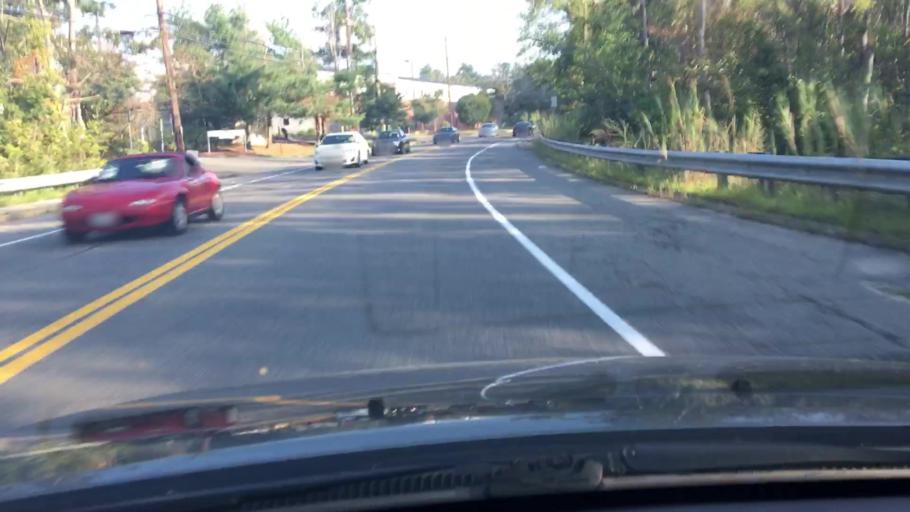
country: US
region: Massachusetts
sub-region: Middlesex County
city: Hopkinton
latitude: 42.2021
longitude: -71.5442
